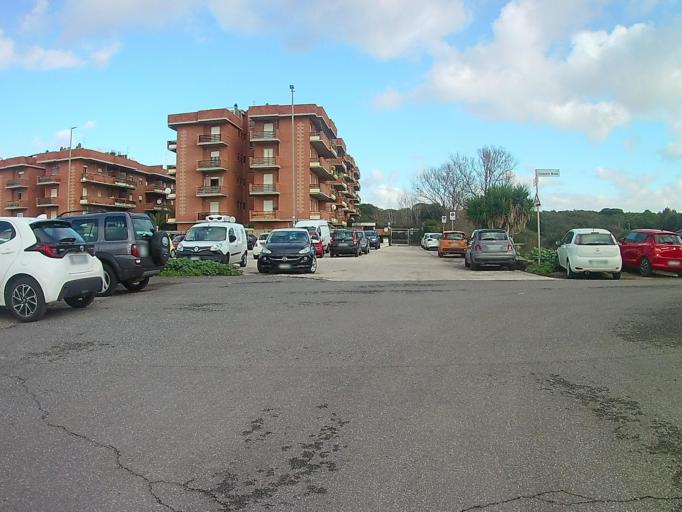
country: IT
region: Latium
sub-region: Citta metropolitana di Roma Capitale
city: Lido di Ostia
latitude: 41.7177
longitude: 12.3113
